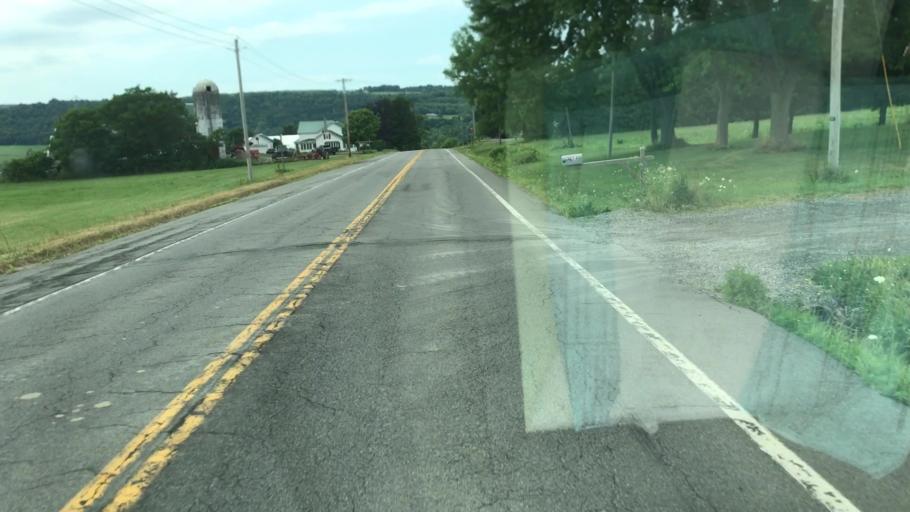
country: US
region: New York
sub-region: Onondaga County
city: Marcellus
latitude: 42.9331
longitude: -76.3158
